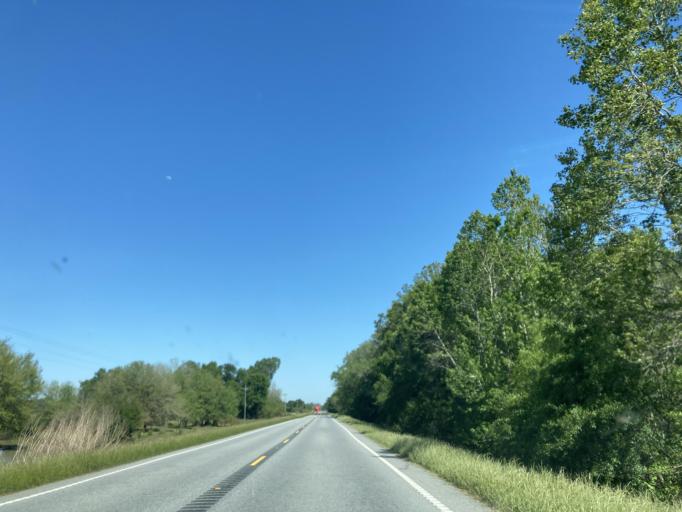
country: US
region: Georgia
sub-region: Miller County
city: Colquitt
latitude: 31.1840
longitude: -84.5639
